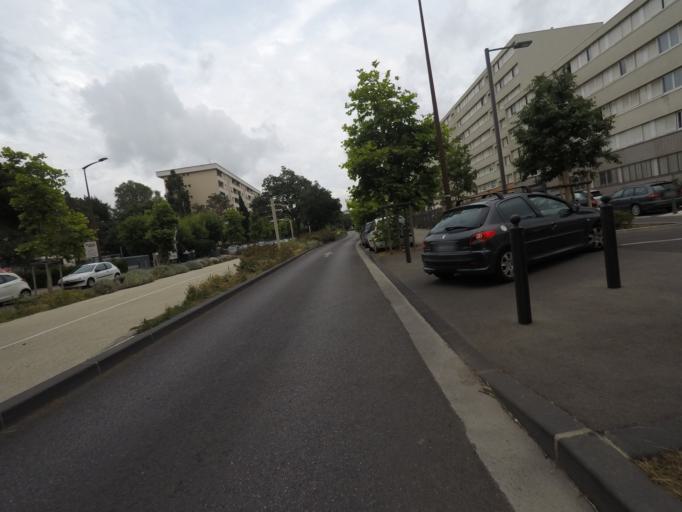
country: FR
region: Provence-Alpes-Cote d'Azur
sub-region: Departement des Bouches-du-Rhone
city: Marseille 09
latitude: 43.2471
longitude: 5.3972
